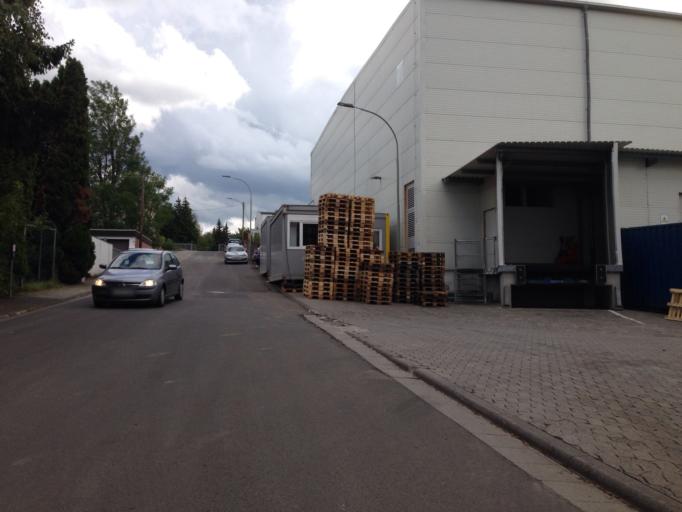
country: DE
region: Hesse
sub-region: Regierungsbezirk Giessen
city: Hungen
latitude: 50.4721
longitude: 8.9106
